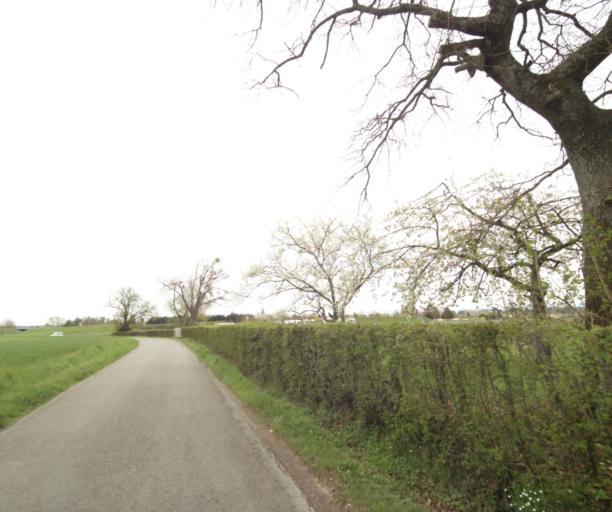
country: FR
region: Bourgogne
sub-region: Departement de Saone-et-Loire
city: Charnay-les-Macon
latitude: 46.3054
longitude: 4.7917
